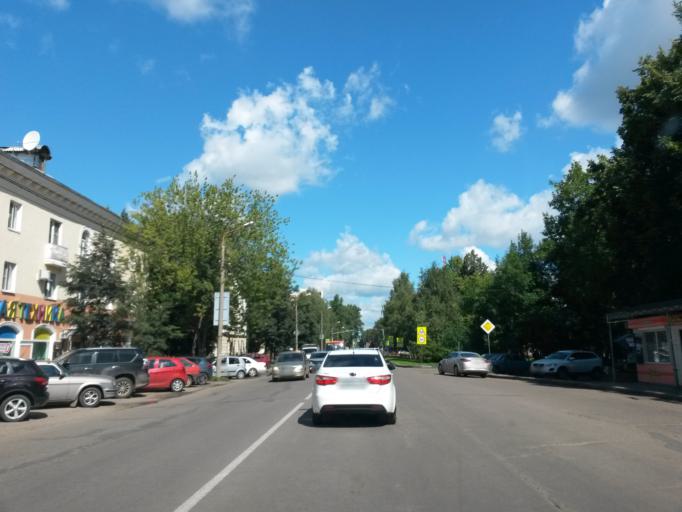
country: RU
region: Jaroslavl
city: Yaroslavl
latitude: 57.5964
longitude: 39.8788
